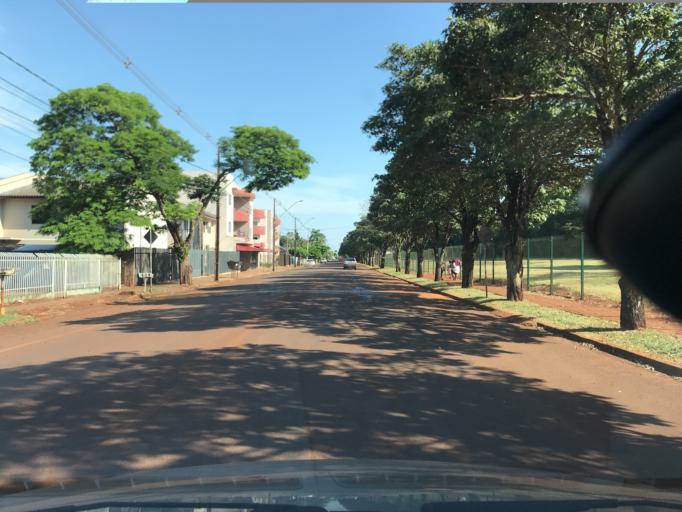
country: BR
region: Parana
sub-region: Palotina
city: Palotina
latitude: -24.2948
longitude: -53.8437
